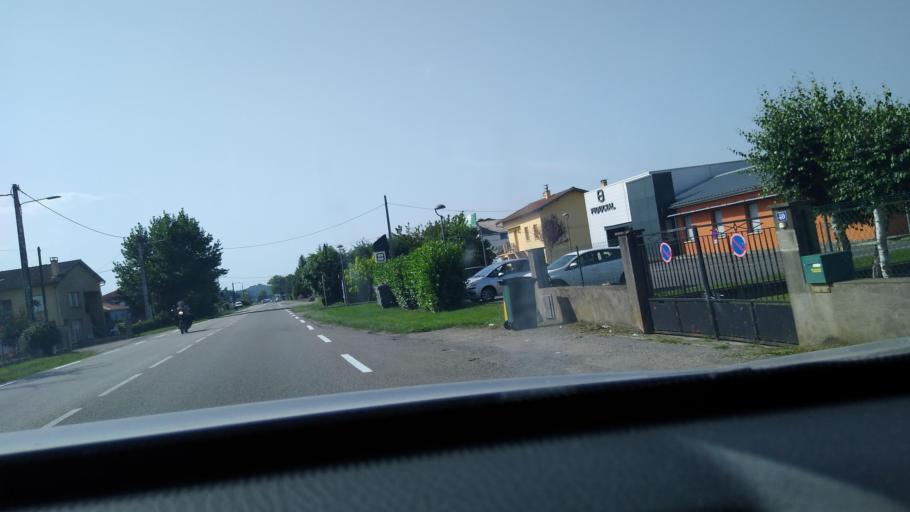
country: FR
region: Midi-Pyrenees
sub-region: Departement de l'Ariege
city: Saint-Lizier
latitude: 43.0129
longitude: 1.1132
